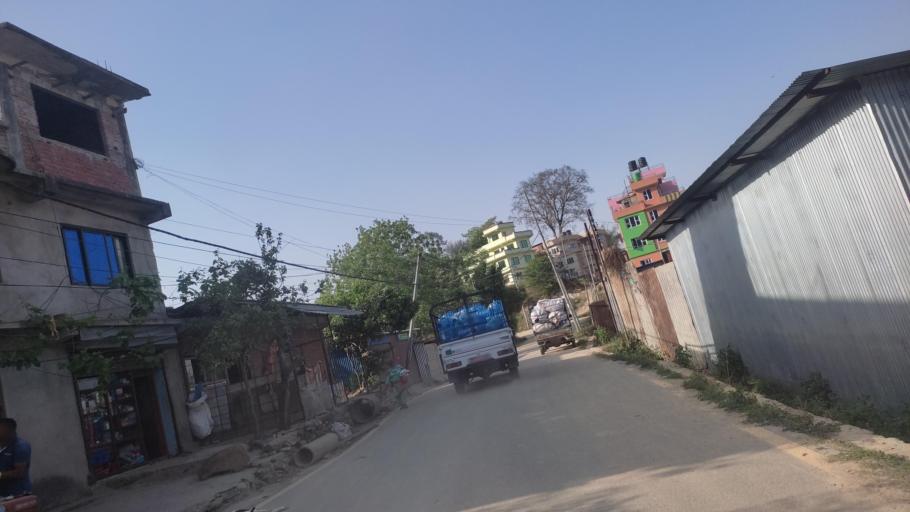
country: NP
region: Central Region
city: Kirtipur
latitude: 27.6523
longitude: 85.2760
